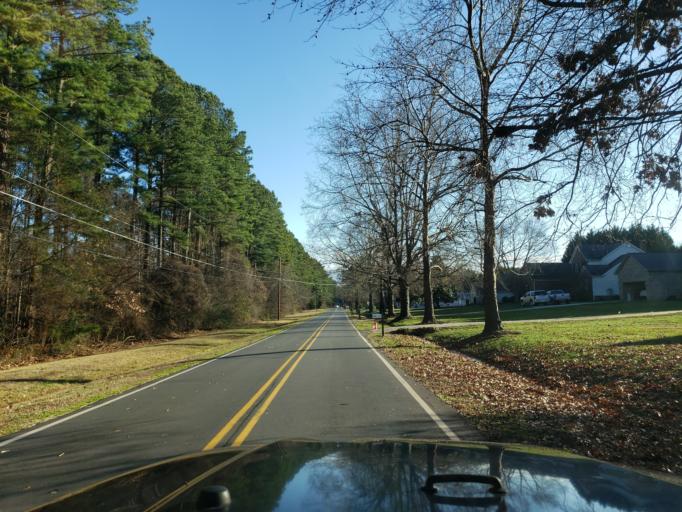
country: US
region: North Carolina
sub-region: Lincoln County
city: Westport
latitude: 35.5196
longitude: -80.9198
